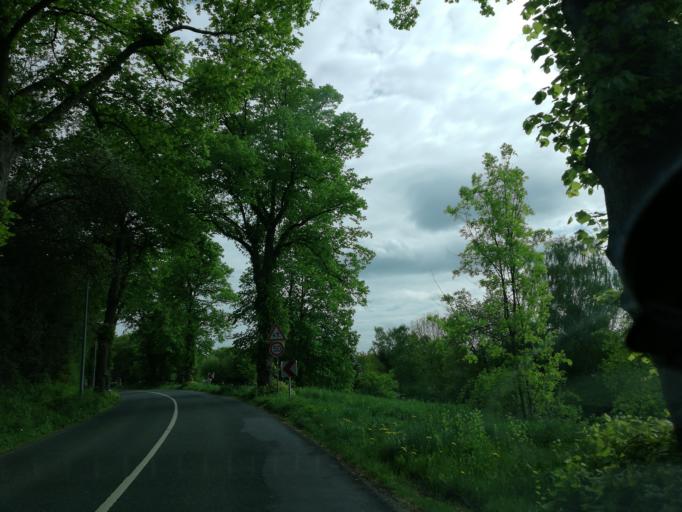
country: DE
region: North Rhine-Westphalia
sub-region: Regierungsbezirk Arnsberg
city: Schwelm
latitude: 51.3112
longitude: 7.2882
